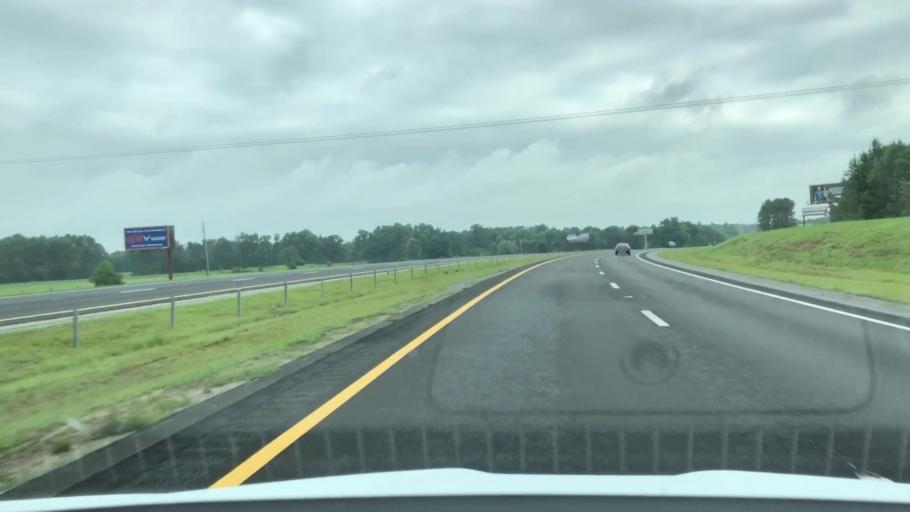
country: US
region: North Carolina
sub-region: Wayne County
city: Fremont
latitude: 35.5075
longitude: -77.9993
